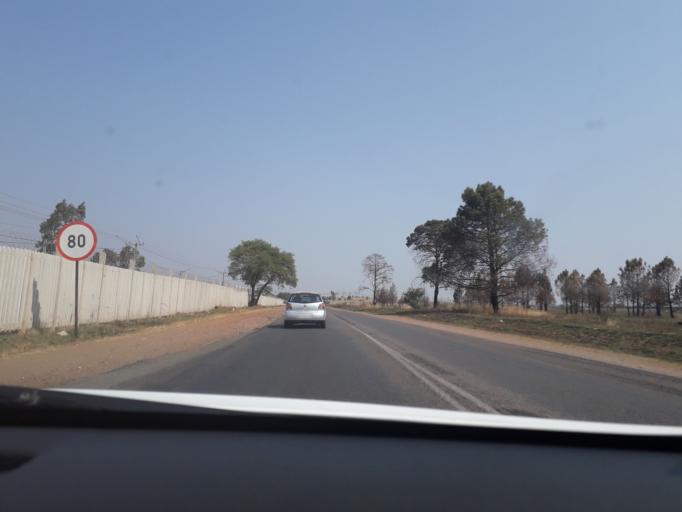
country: ZA
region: Gauteng
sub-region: City of Tshwane Metropolitan Municipality
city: Centurion
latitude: -25.8976
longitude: 28.2250
